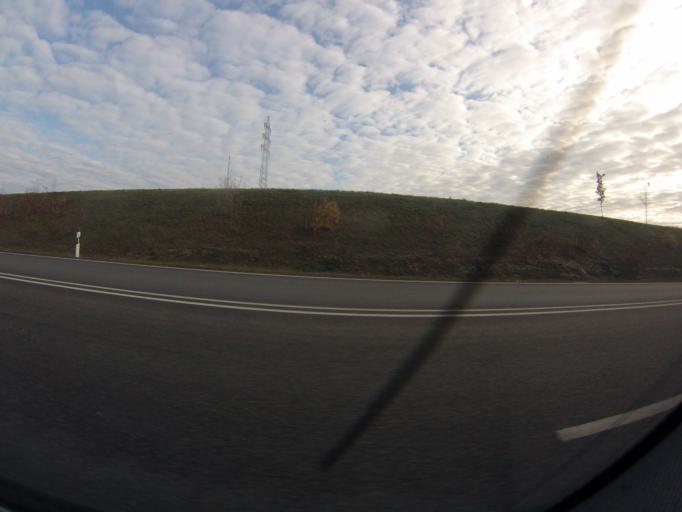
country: DE
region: Thuringia
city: Gossnitz
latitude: 50.8928
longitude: 12.4427
